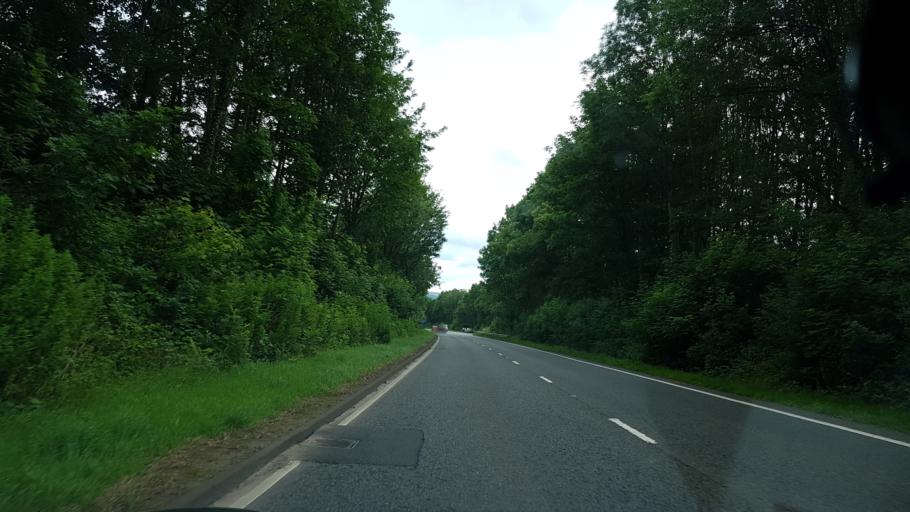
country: GB
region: Wales
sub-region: Monmouthshire
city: Abergavenny
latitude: 51.8218
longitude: -3.0074
